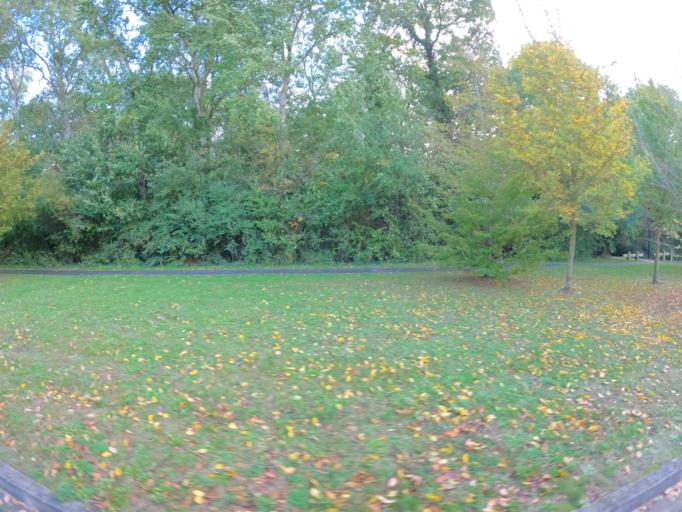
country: FR
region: Ile-de-France
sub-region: Departement de Seine-et-Marne
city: Magny-le-Hongre
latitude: 48.8760
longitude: 2.8135
